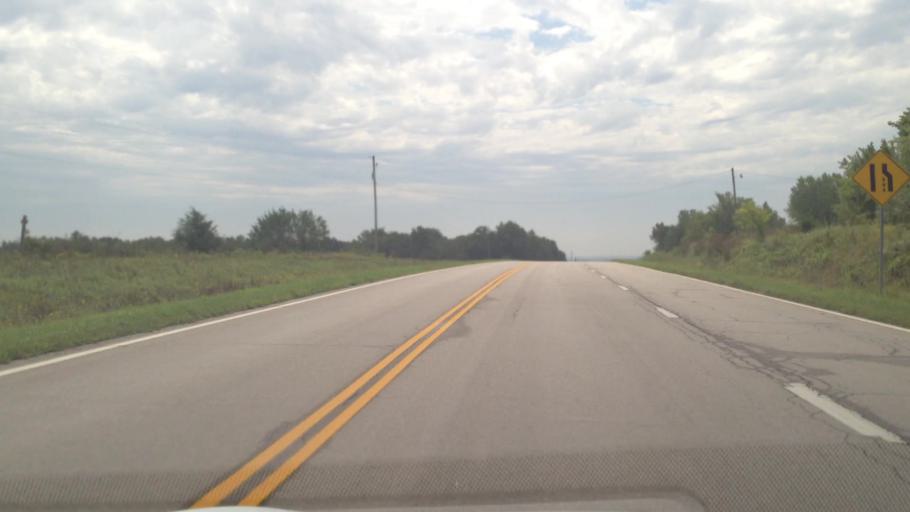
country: US
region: Kansas
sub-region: Bourbon County
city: Fort Scott
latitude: 37.8270
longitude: -94.9792
